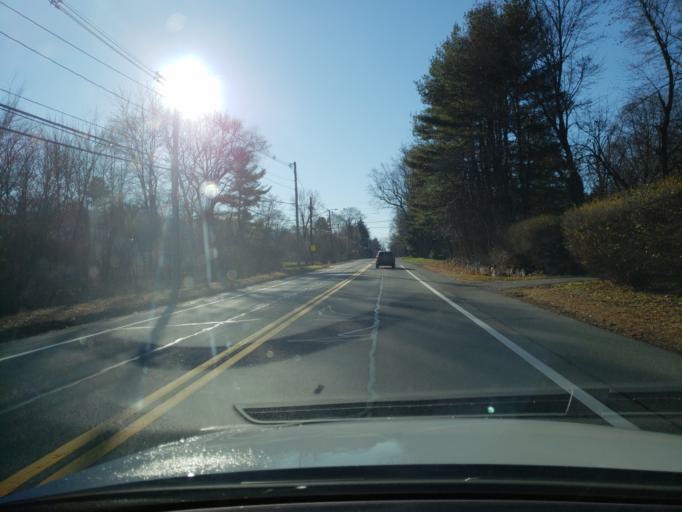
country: US
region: Massachusetts
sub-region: Essex County
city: Andover
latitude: 42.6396
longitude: -71.1305
